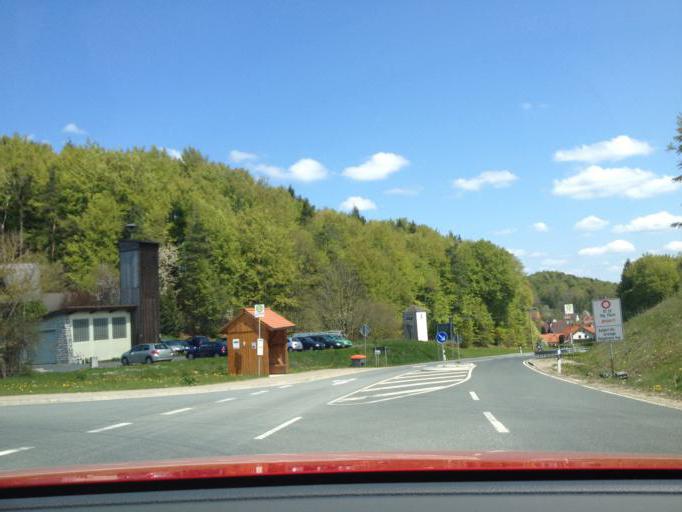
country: DE
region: Bavaria
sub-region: Regierungsbezirk Mittelfranken
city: Kirchensittenbach
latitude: 49.6294
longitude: 11.4141
